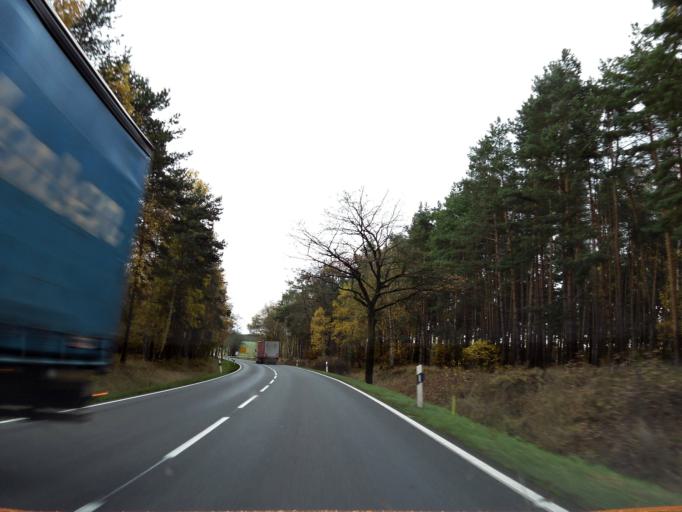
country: DE
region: Saxony-Anhalt
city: Kalbe
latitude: 52.6444
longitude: 11.3016
